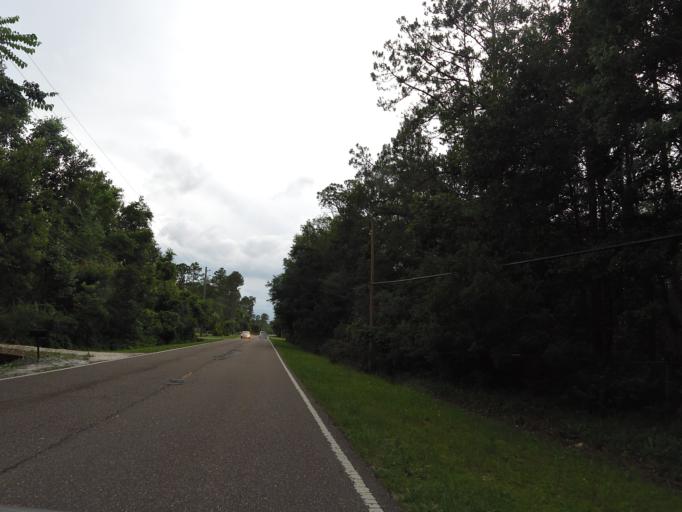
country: US
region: Florida
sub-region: Nassau County
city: Nassau Village-Ratliff
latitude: 30.5261
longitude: -81.7376
